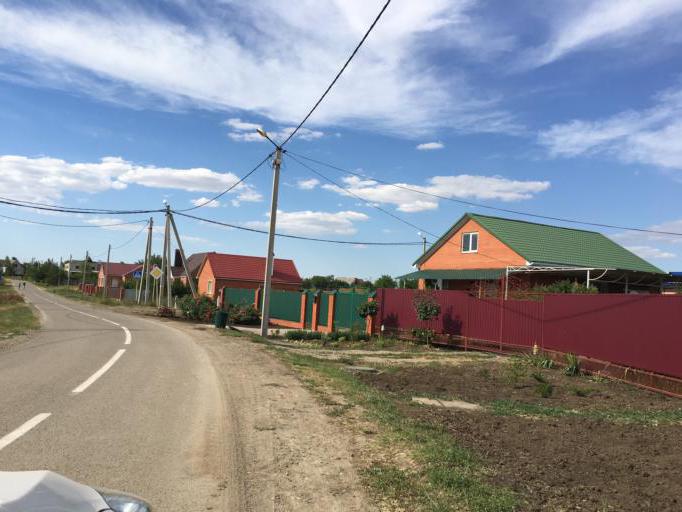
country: RU
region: Krasnodarskiy
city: Kushchevskaya
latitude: 46.5532
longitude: 39.6743
